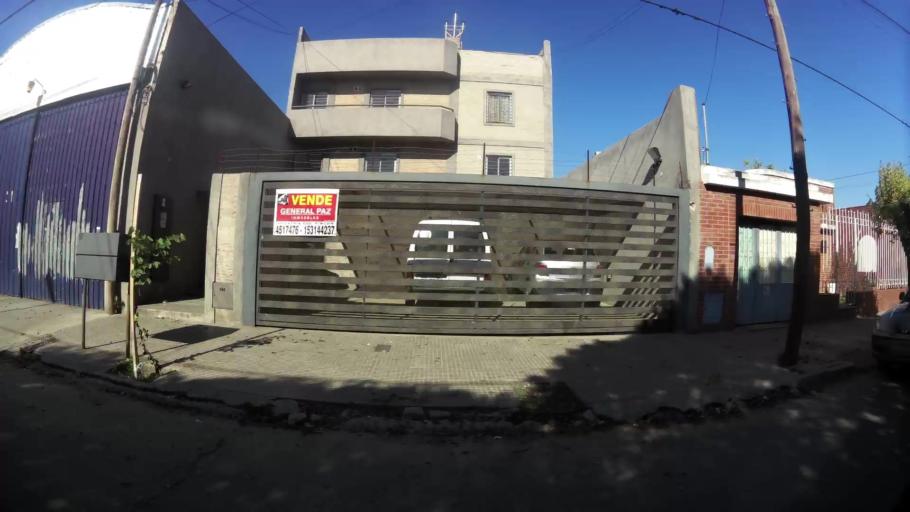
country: AR
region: Cordoba
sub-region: Departamento de Capital
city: Cordoba
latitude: -31.3958
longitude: -64.1534
